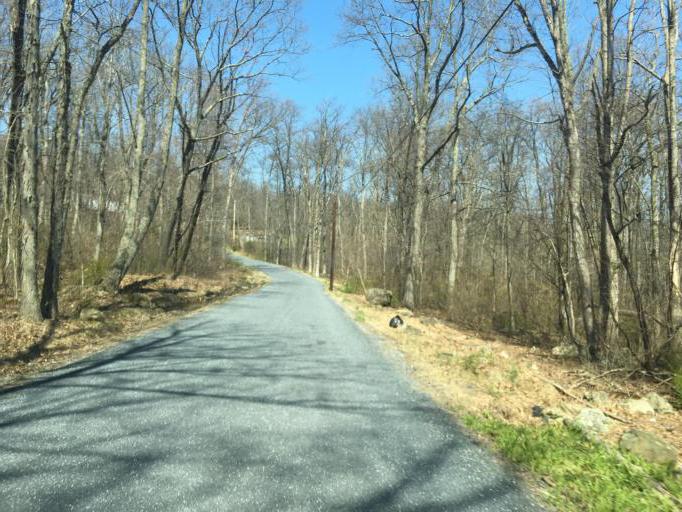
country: US
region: Maryland
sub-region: Washington County
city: Smithsburg
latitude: 39.6348
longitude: -77.5229
